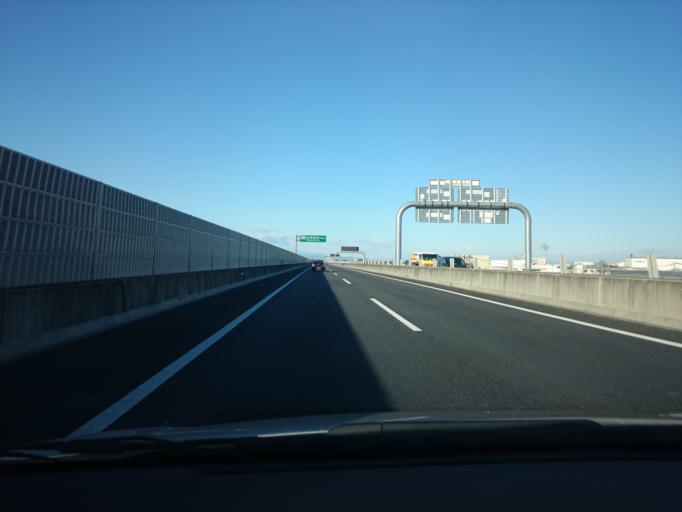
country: JP
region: Saitama
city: Kukichuo
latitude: 36.0501
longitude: 139.6459
